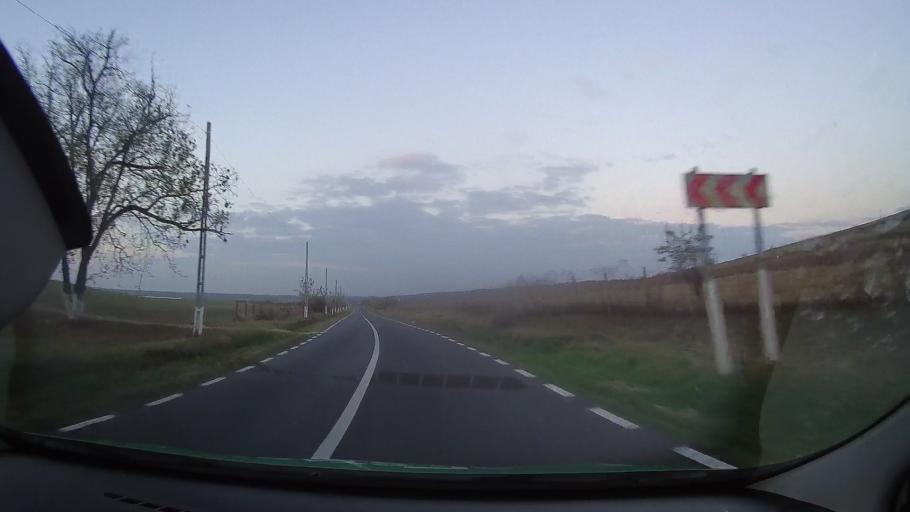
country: RO
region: Constanta
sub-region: Comuna Oltina
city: Oltina
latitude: 44.1512
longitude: 27.6677
